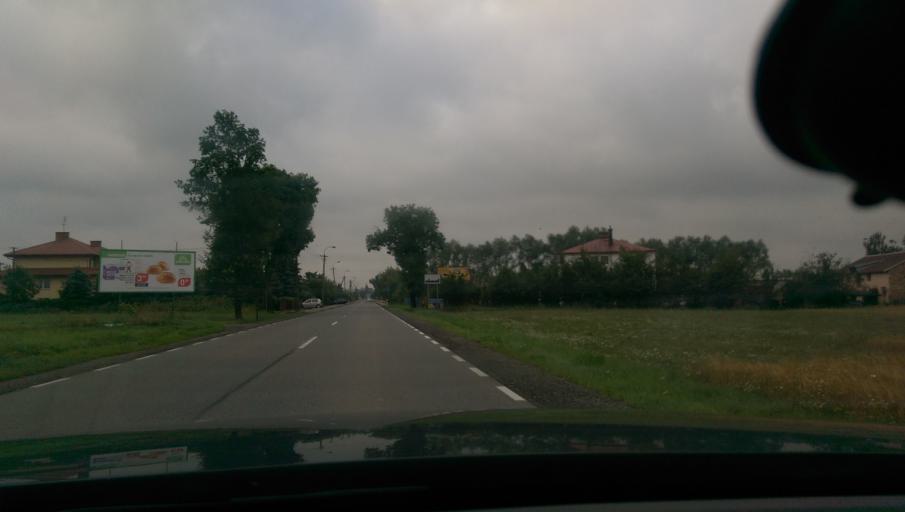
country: PL
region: Masovian Voivodeship
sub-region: Powiat przasnyski
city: Przasnysz
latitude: 53.0312
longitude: 20.8788
